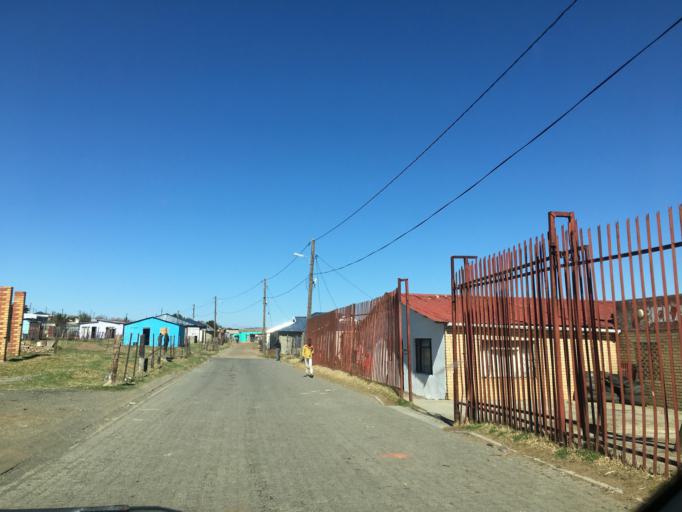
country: ZA
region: Eastern Cape
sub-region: Chris Hani District Municipality
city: Elliot
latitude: -31.3353
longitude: 27.8599
